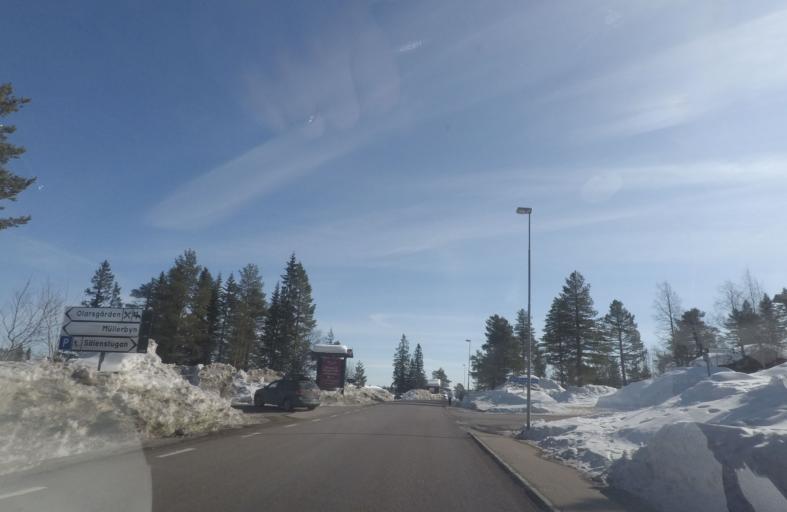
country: SE
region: Dalarna
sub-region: Malung-Saelens kommun
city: Malung
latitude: 61.1670
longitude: 13.1716
